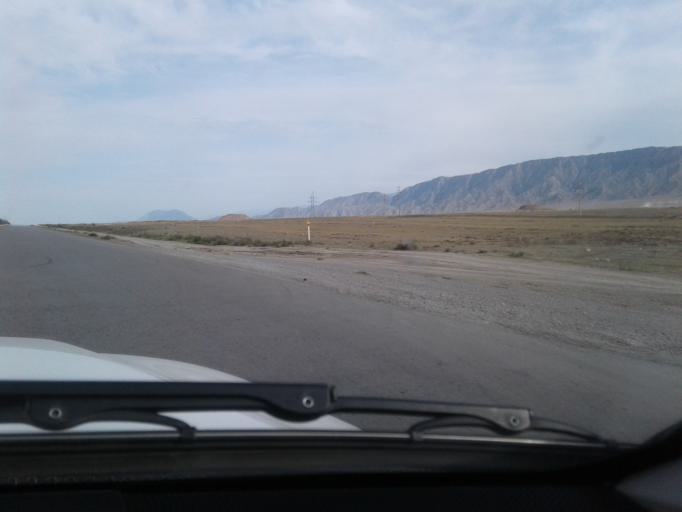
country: TM
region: Ahal
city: Baharly
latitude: 38.2286
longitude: 57.7892
